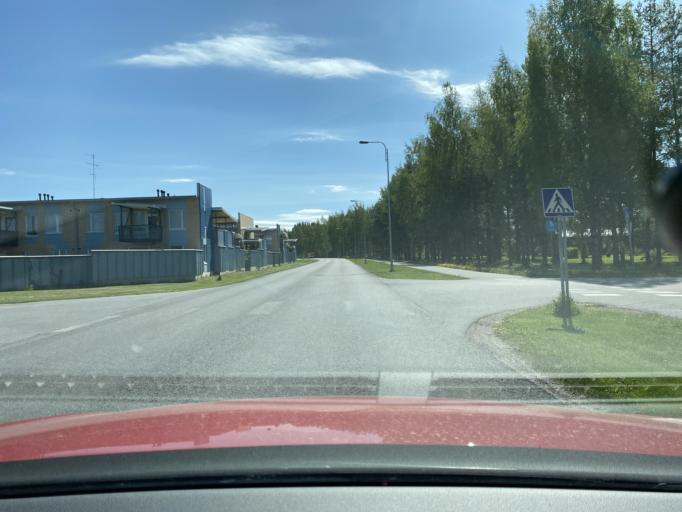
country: FI
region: Satakunta
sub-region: Rauma
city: Eura
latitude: 61.1248
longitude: 22.1528
